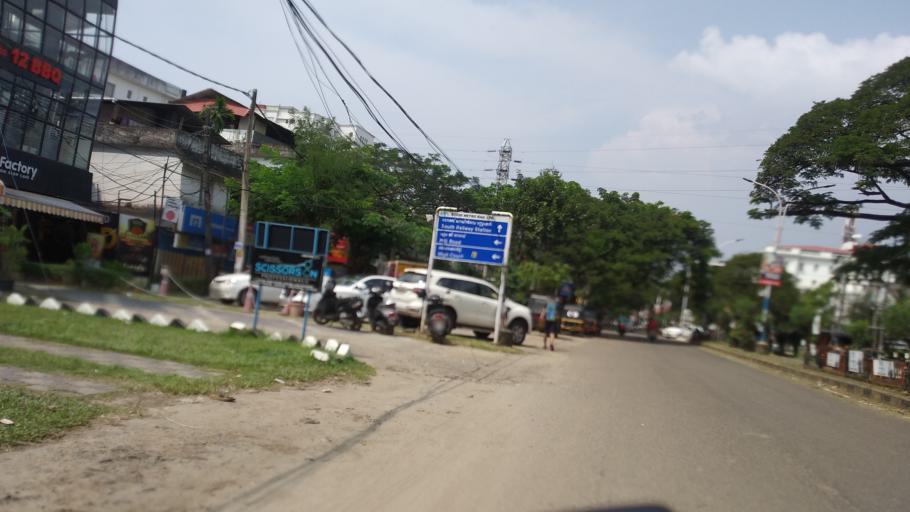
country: IN
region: Kerala
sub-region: Ernakulam
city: Cochin
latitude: 9.9554
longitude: 76.2965
